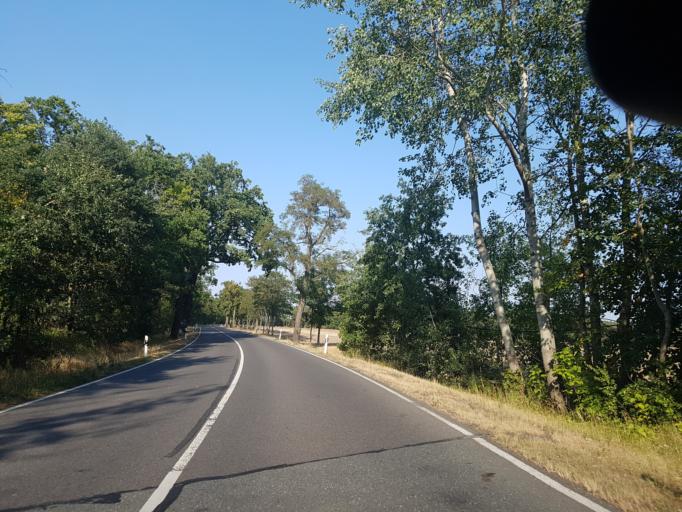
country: DE
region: Brandenburg
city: Falkenberg
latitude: 51.5429
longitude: 13.2331
